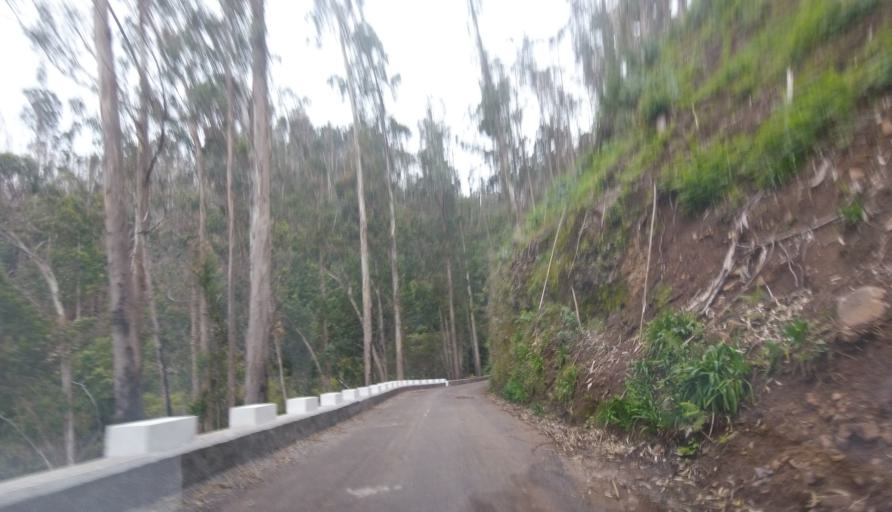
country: PT
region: Madeira
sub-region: Funchal
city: Nossa Senhora do Monte
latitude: 32.6897
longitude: -16.8894
